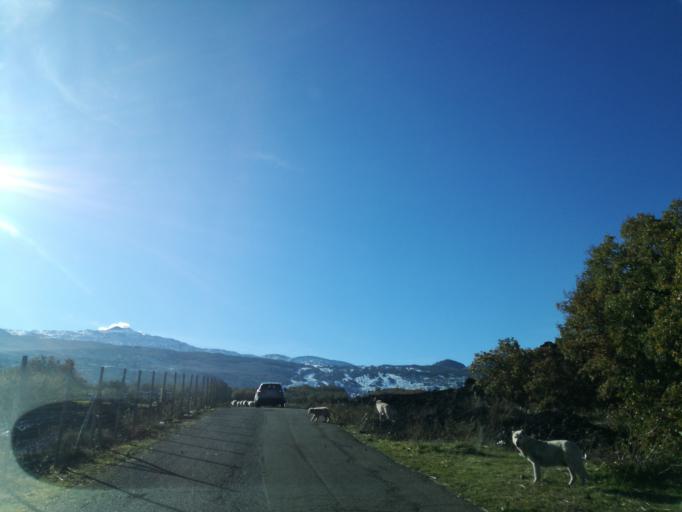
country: IT
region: Sicily
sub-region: Catania
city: Randazzo
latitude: 37.8631
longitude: 14.9796
